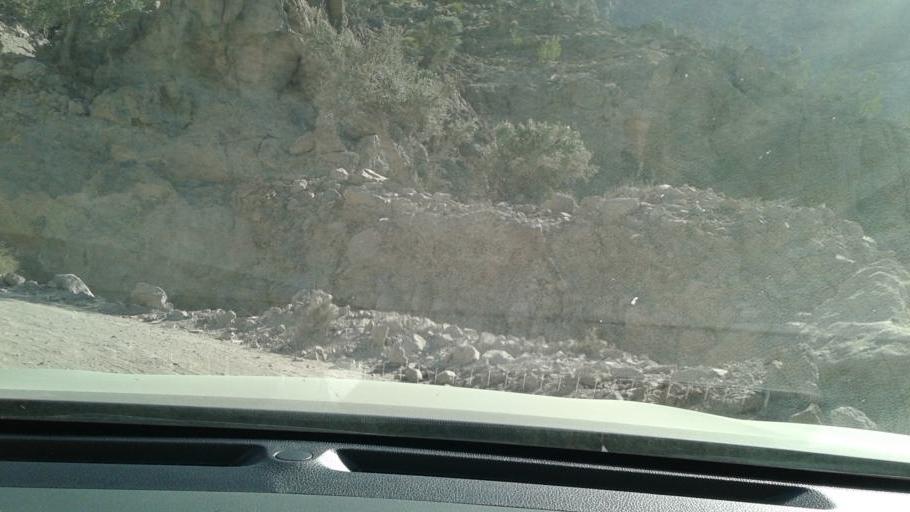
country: OM
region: Al Batinah
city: Bayt al `Awabi
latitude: 23.1758
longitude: 57.4132
